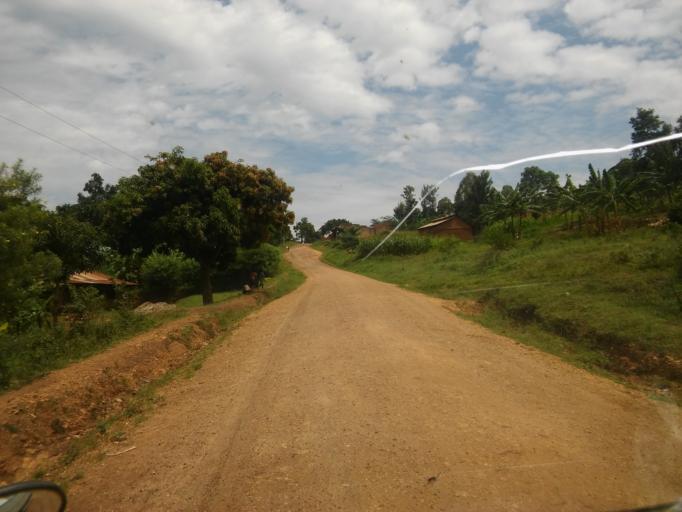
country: UG
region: Eastern Region
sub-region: Bududa District
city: Bududa
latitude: 0.9213
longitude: 34.2816
